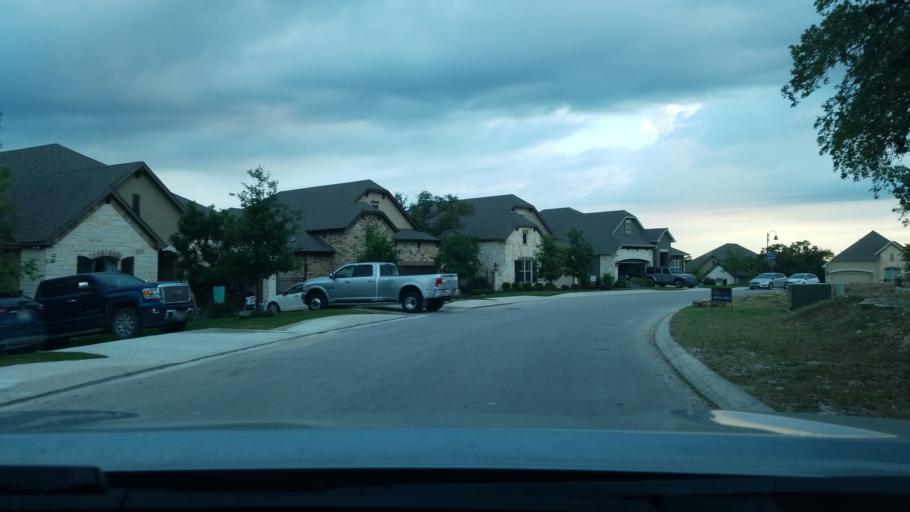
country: US
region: Texas
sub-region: Bexar County
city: Timberwood Park
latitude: 29.7160
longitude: -98.4596
